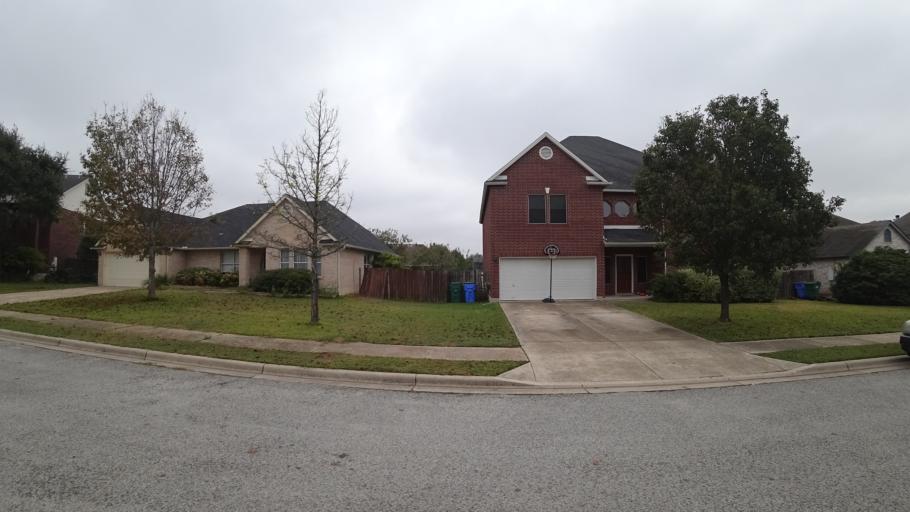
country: US
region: Texas
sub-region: Travis County
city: Pflugerville
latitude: 30.4255
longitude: -97.6216
